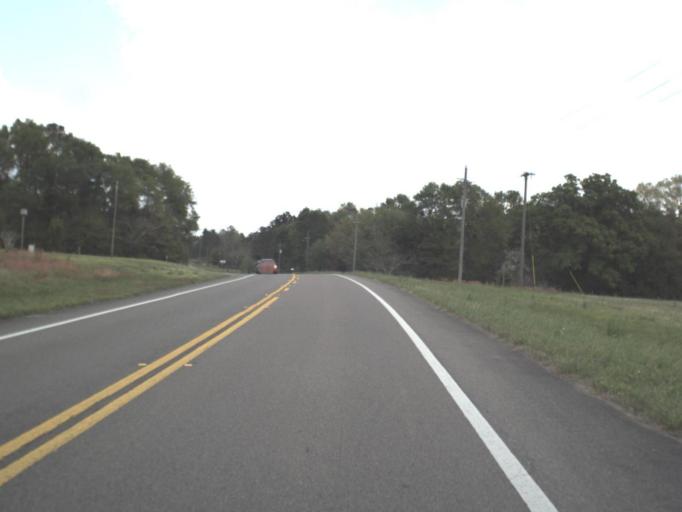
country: US
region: Florida
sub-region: Okaloosa County
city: Crestview
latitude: 30.8678
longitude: -86.6678
